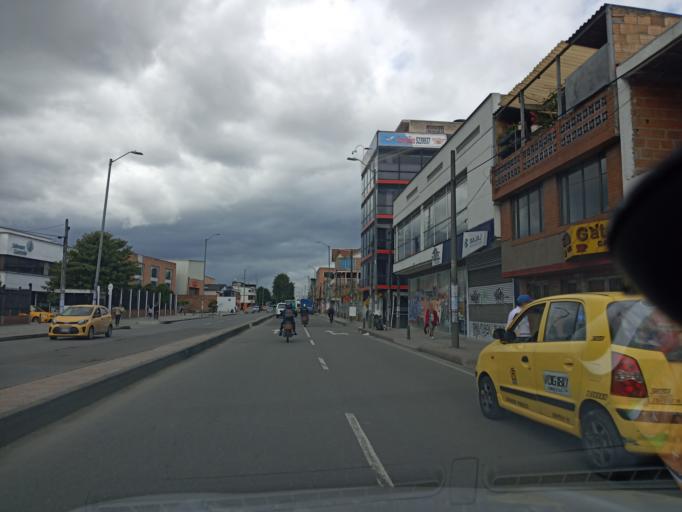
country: CO
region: Cundinamarca
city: Funza
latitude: 4.6852
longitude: -74.1311
